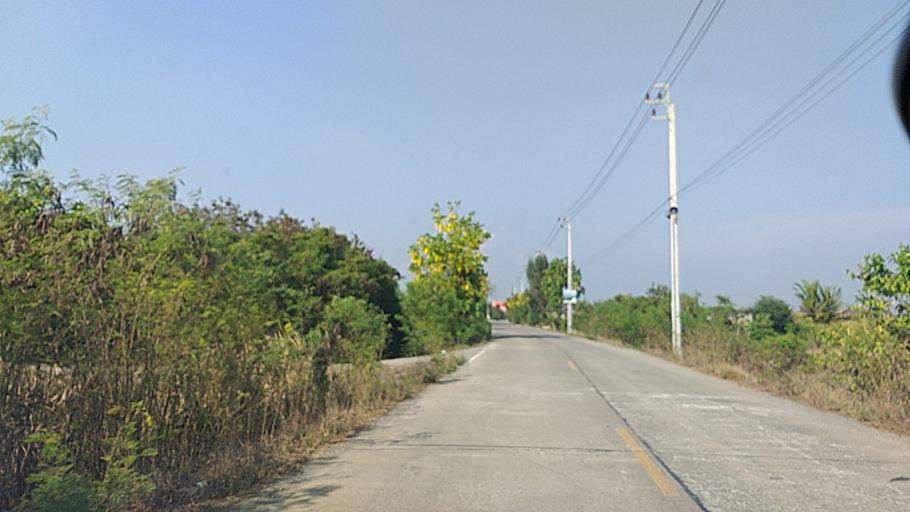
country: TH
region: Nonthaburi
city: Sai Noi
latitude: 13.9383
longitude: 100.3242
